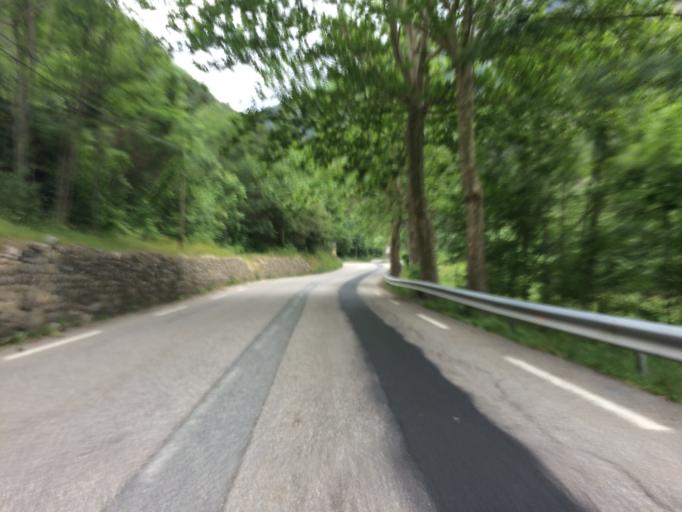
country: FR
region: Provence-Alpes-Cote d'Azur
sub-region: Departement des Alpes-Maritimes
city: Tende
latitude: 44.1073
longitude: 7.5719
